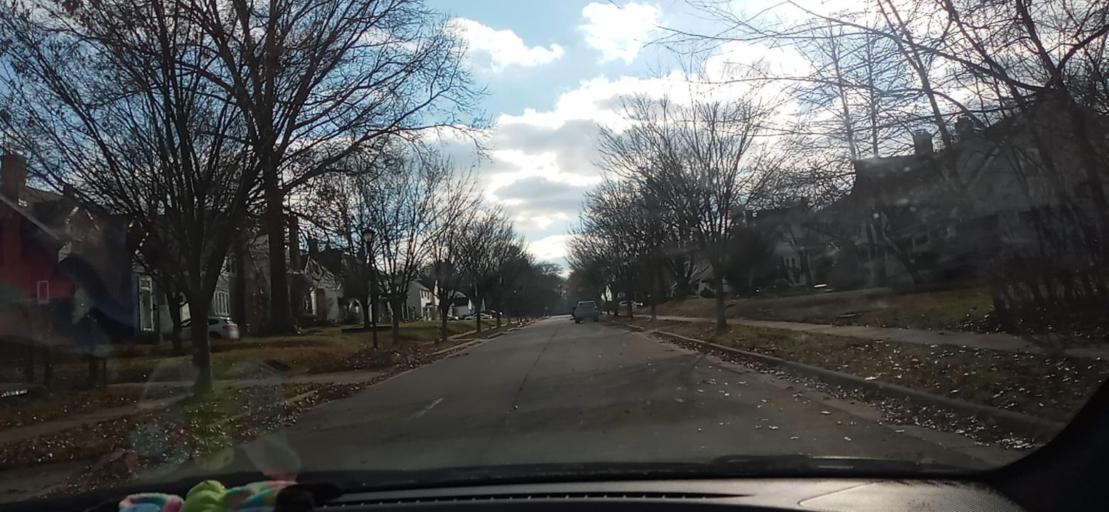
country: US
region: Ohio
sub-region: Summit County
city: Akron
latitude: 41.0945
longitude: -81.5670
